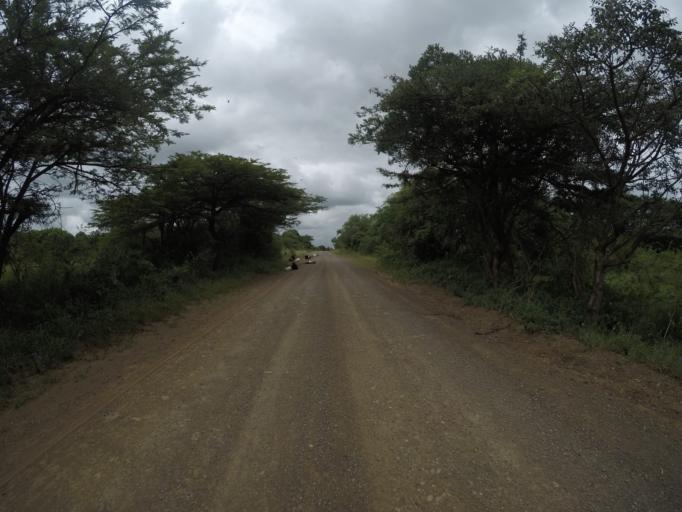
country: ZA
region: KwaZulu-Natal
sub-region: uThungulu District Municipality
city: Empangeni
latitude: -28.5606
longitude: 31.8758
